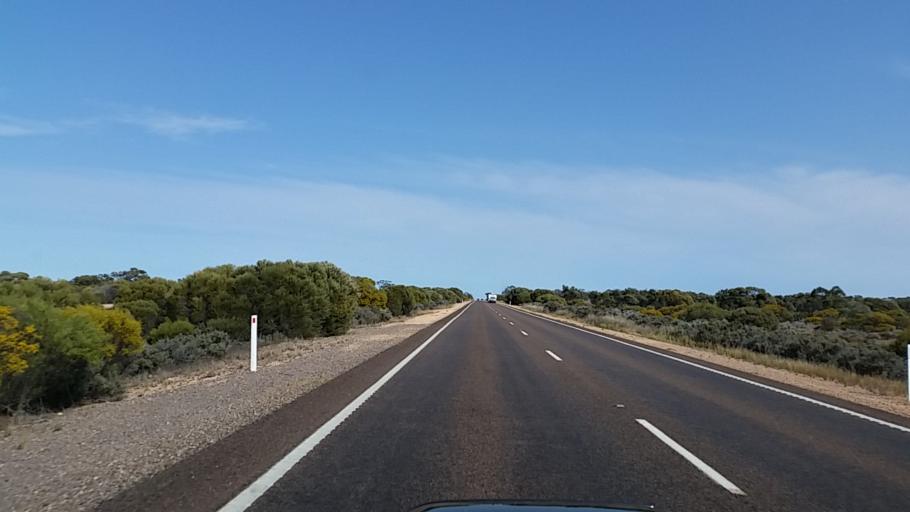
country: AU
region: South Australia
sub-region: Whyalla
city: Whyalla
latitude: -32.7982
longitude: 137.5387
